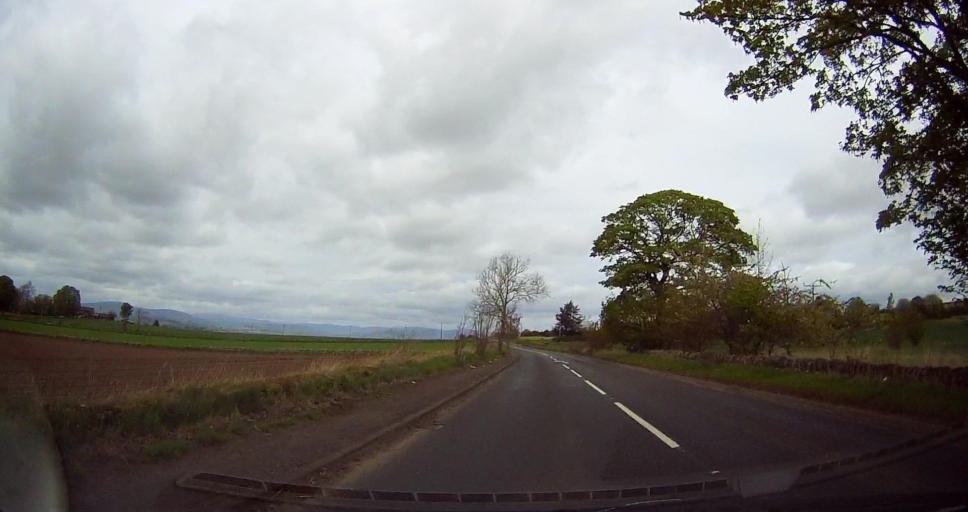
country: GB
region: Scotland
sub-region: Angus
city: Forfar
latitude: 56.6224
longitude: -2.8995
